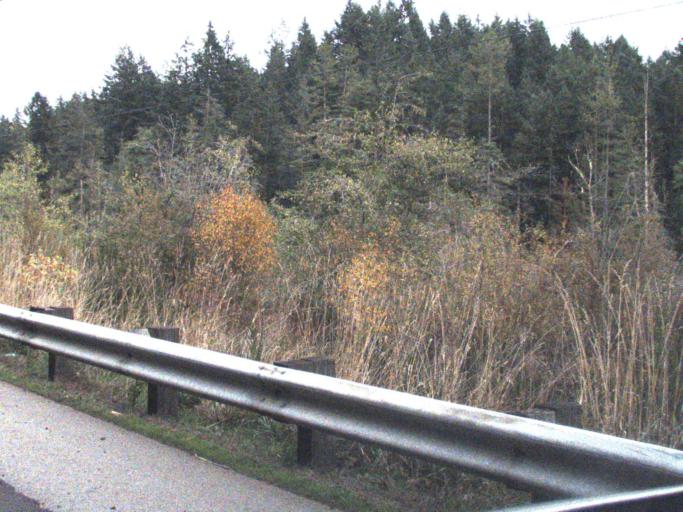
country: US
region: Washington
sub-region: Island County
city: Langley
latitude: 48.0018
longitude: -122.4458
